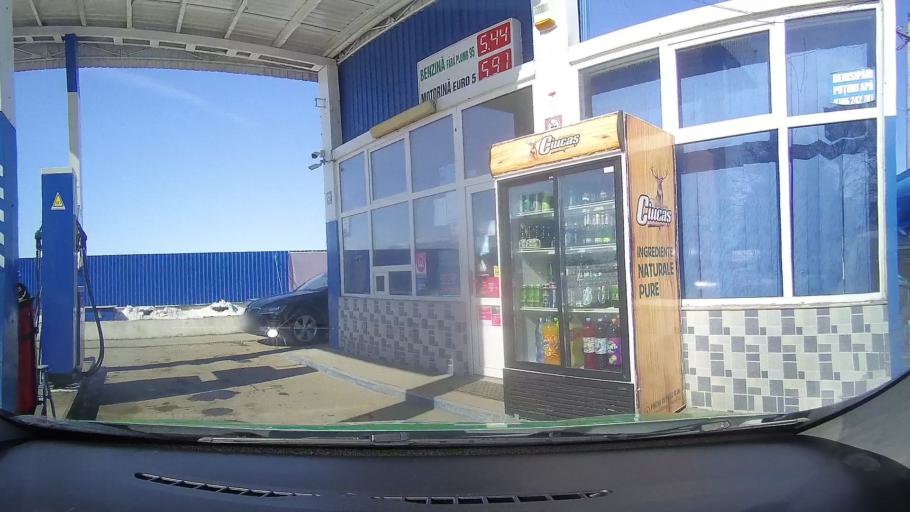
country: RO
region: Brasov
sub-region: Comuna Recea
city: Recea
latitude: 45.7343
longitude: 24.9334
